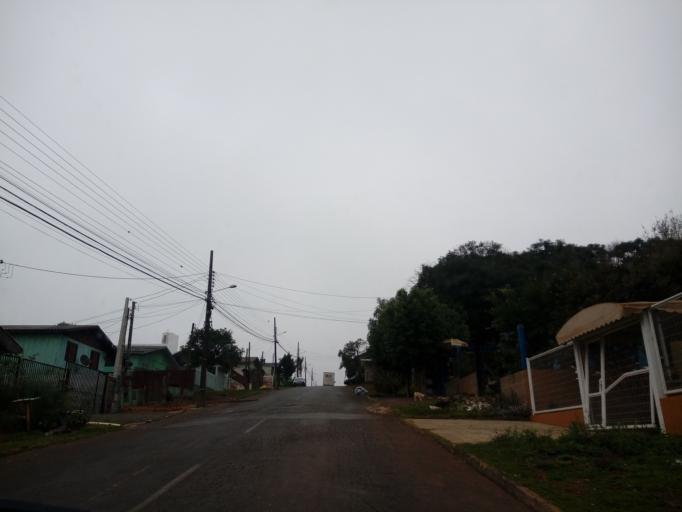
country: BR
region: Santa Catarina
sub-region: Chapeco
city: Chapeco
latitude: -27.1023
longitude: -52.6701
